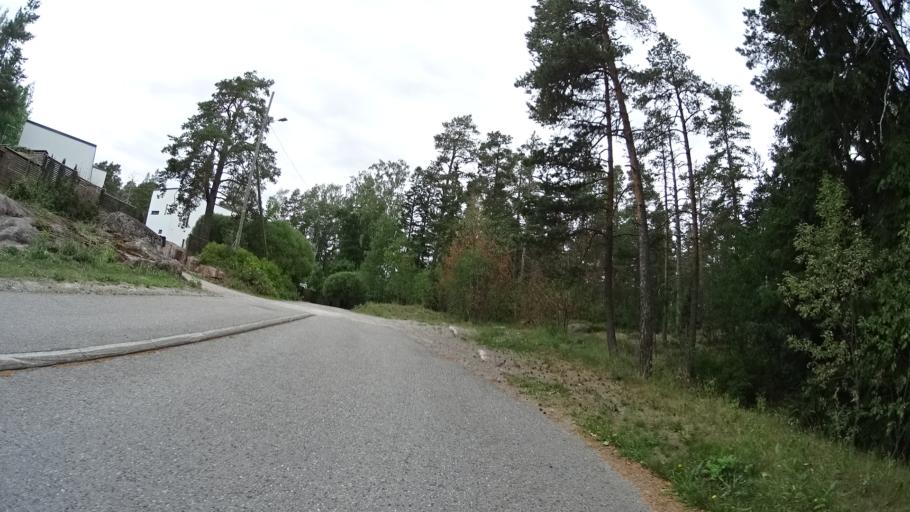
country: FI
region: Uusimaa
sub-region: Helsinki
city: Espoo
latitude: 60.1336
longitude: 24.6712
